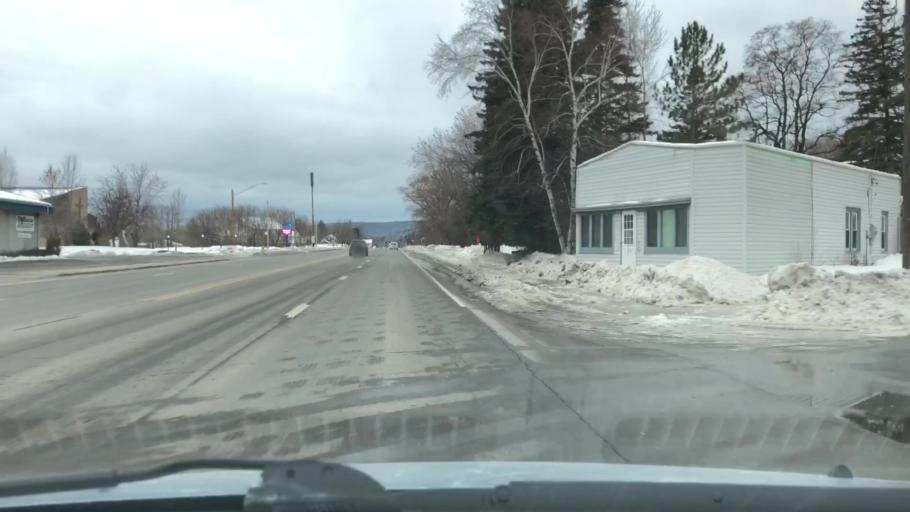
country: US
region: Minnesota
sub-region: Saint Louis County
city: Proctor
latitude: 46.7300
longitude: -92.1819
